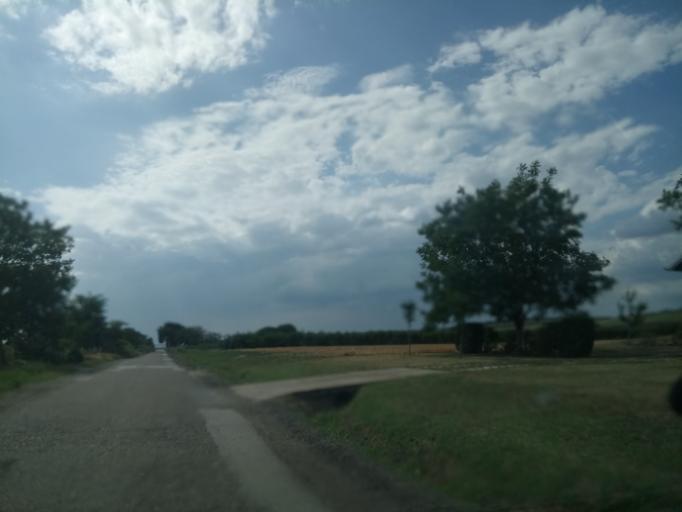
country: RS
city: Novi Slankamen
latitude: 45.1356
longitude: 20.2408
